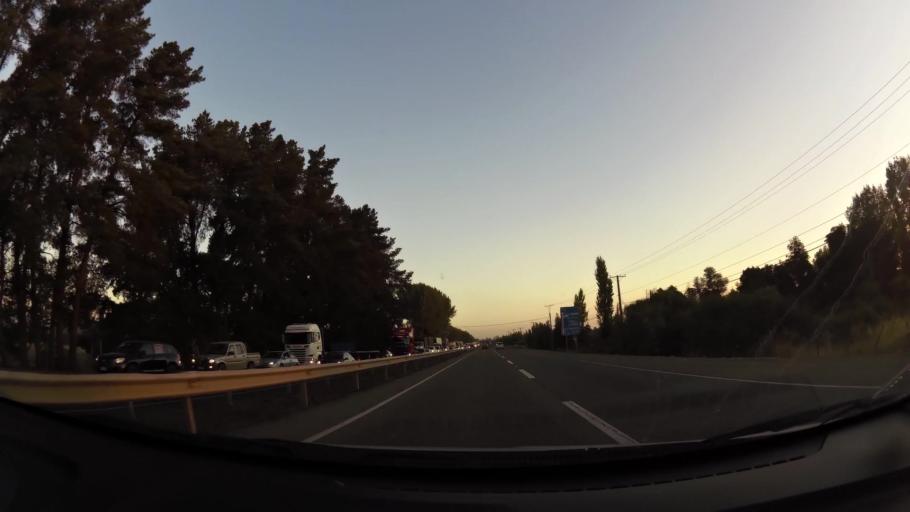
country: CL
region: Maule
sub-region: Provincia de Linares
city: Linares
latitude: -35.7526
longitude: -71.6730
